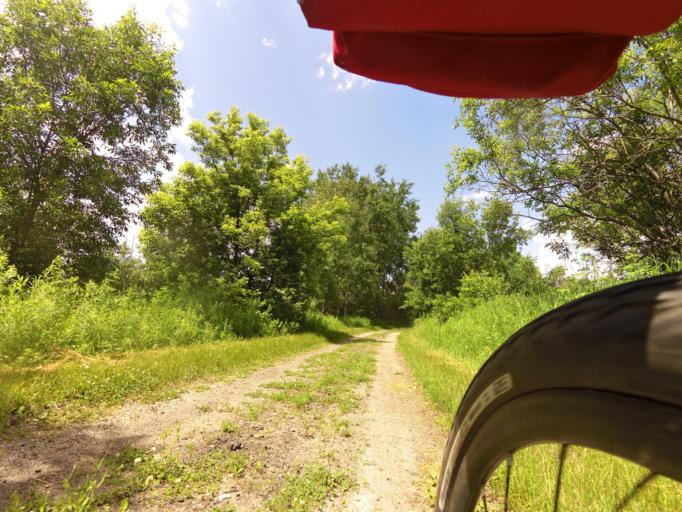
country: CA
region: Quebec
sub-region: Outaouais
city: Maniwaki
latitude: 46.0608
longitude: -76.1095
